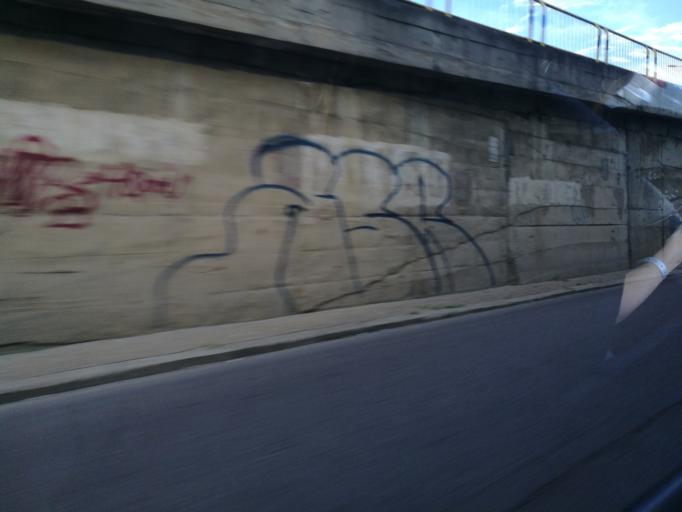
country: RO
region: Constanta
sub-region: Municipiul Constanta
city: Constanta
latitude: 44.1509
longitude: 28.6239
